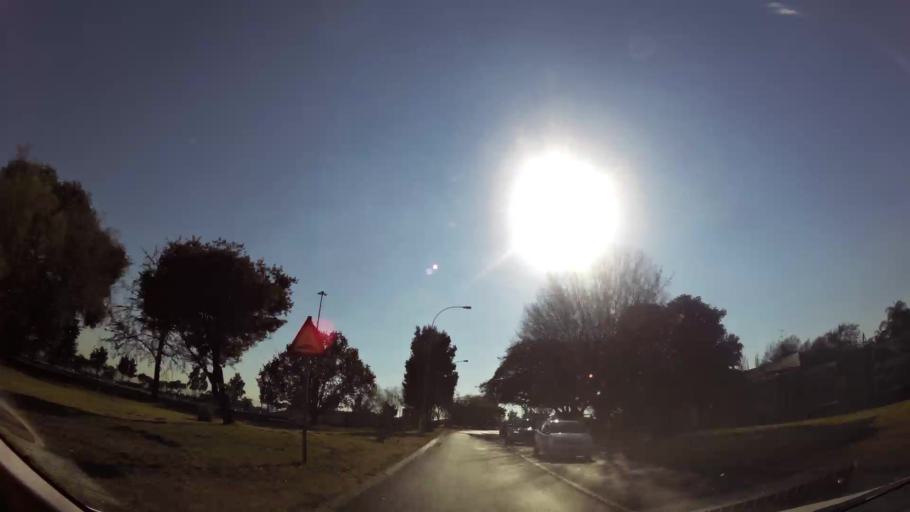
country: ZA
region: Gauteng
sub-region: Ekurhuleni Metropolitan Municipality
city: Germiston
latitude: -26.1694
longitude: 28.1361
